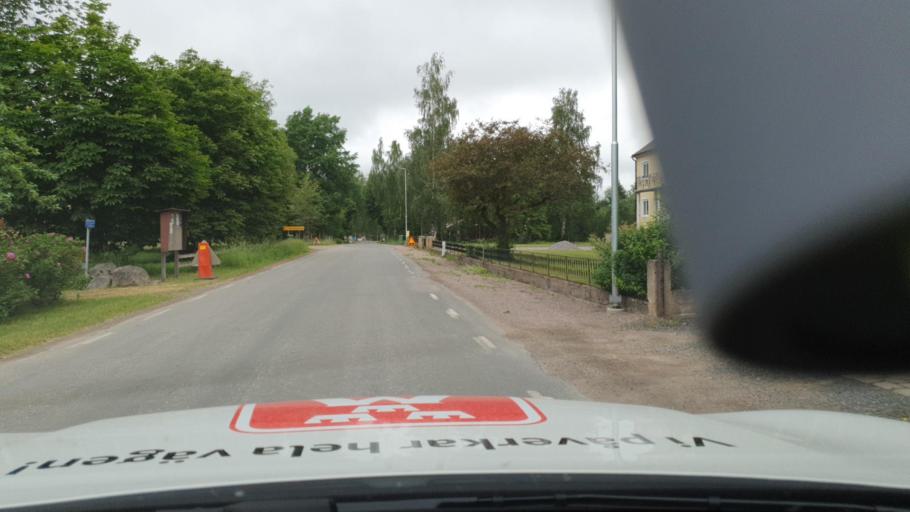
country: SE
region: Vaestra Goetaland
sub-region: Tibro Kommun
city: Tibro
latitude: 58.3703
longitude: 14.0492
